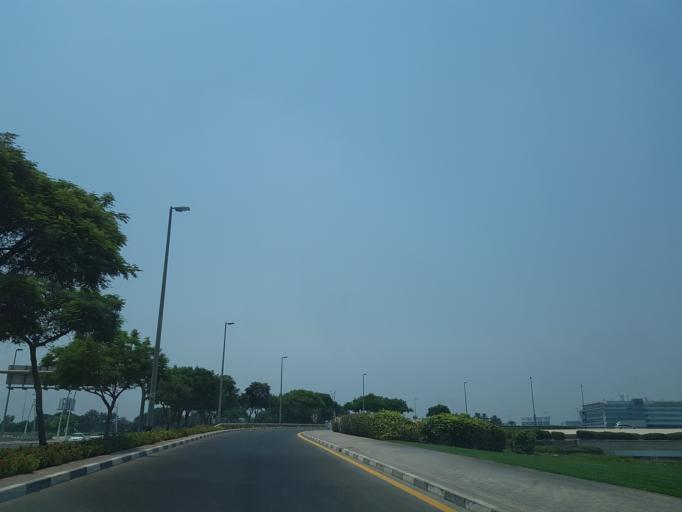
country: AE
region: Ash Shariqah
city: Sharjah
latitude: 25.2363
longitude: 55.3441
